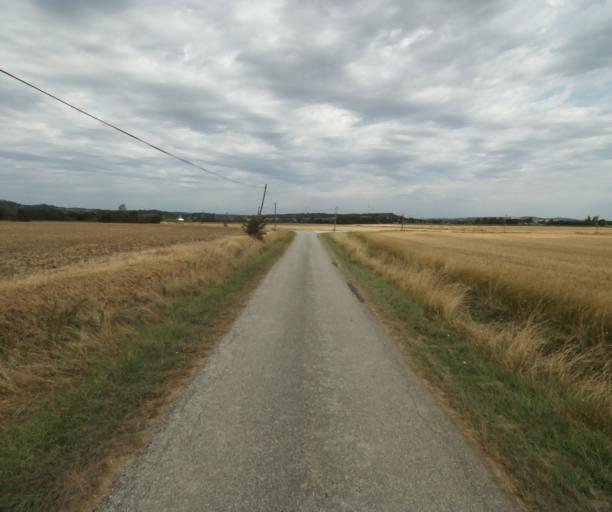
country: FR
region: Midi-Pyrenees
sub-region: Departement de la Haute-Garonne
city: Saint-Felix-Lauragais
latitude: 43.4381
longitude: 1.9340
